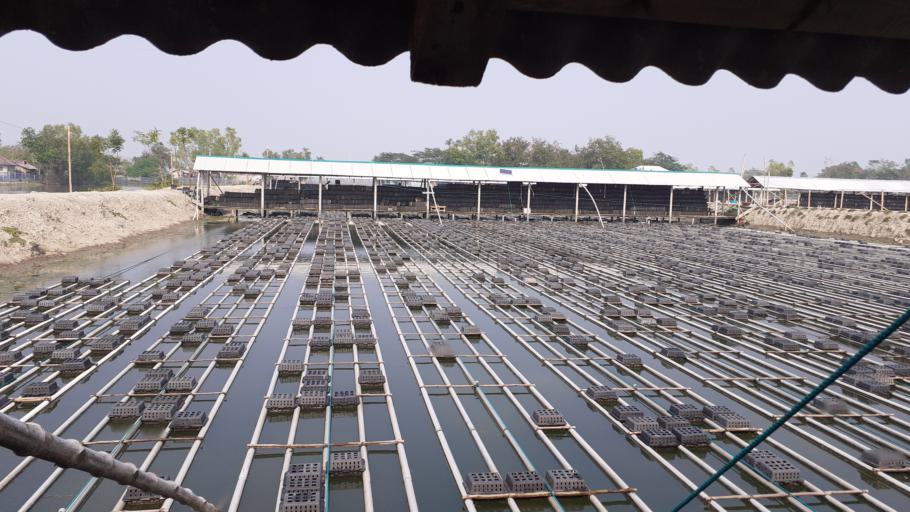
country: IN
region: West Bengal
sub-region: North 24 Parganas
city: Taki
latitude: 22.2704
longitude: 89.2118
